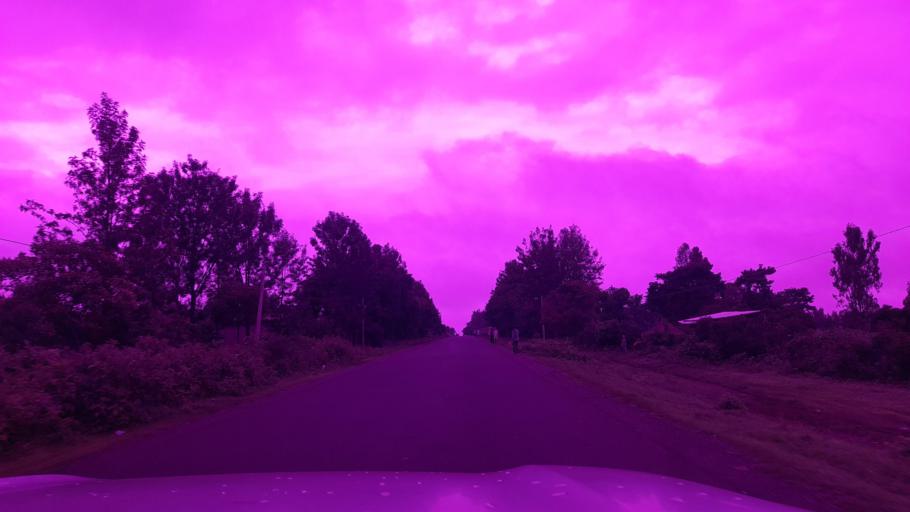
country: ET
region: Oromiya
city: Waliso
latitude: 8.2674
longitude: 37.6573
